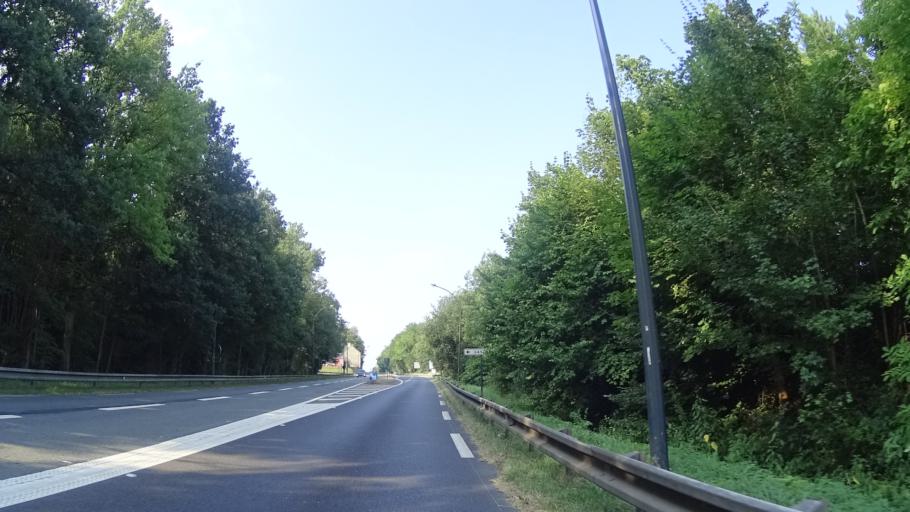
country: FR
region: Ile-de-France
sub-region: Departement du Val-d'Oise
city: Luzarches
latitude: 49.1035
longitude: 2.4237
